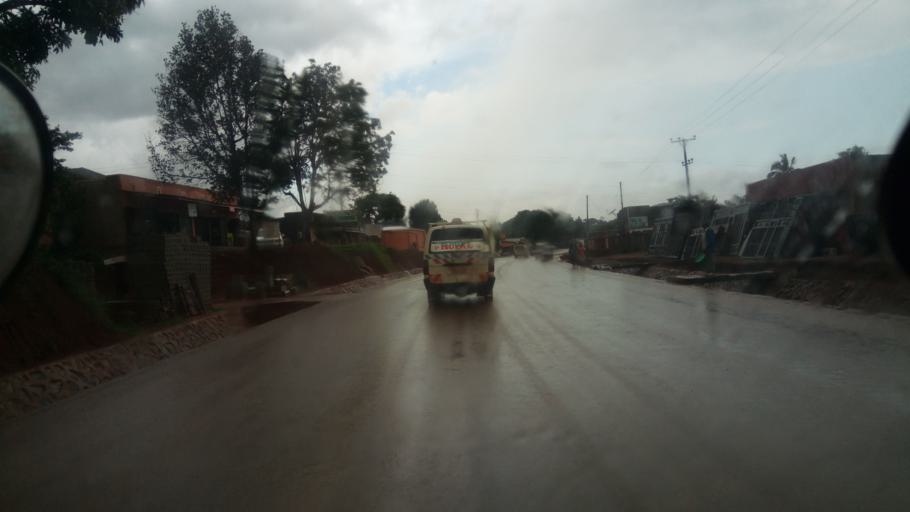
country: UG
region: Central Region
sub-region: Wakiso District
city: Wakiso
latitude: 0.4035
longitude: 32.4752
